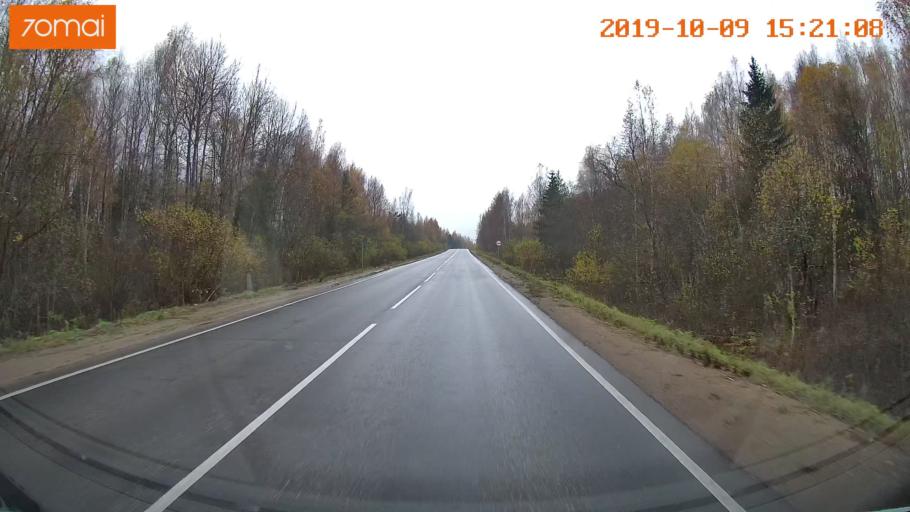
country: RU
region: Kostroma
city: Susanino
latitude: 58.0568
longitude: 41.5254
